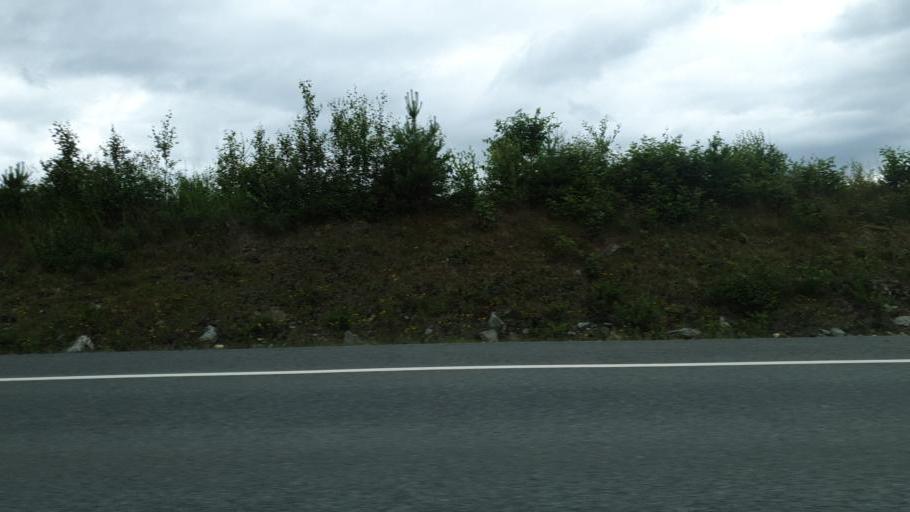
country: NO
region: Sor-Trondelag
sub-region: Rennebu
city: Berkak
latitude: 62.7922
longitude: 10.0055
